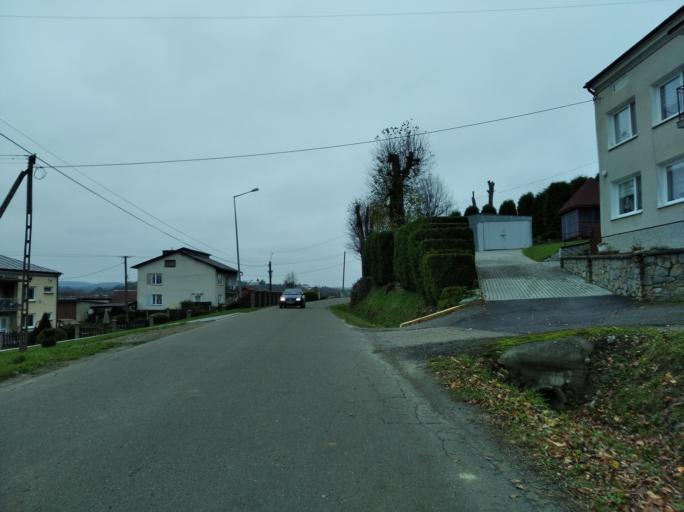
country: PL
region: Subcarpathian Voivodeship
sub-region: Powiat strzyzowski
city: Frysztak
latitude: 49.8329
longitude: 21.6289
